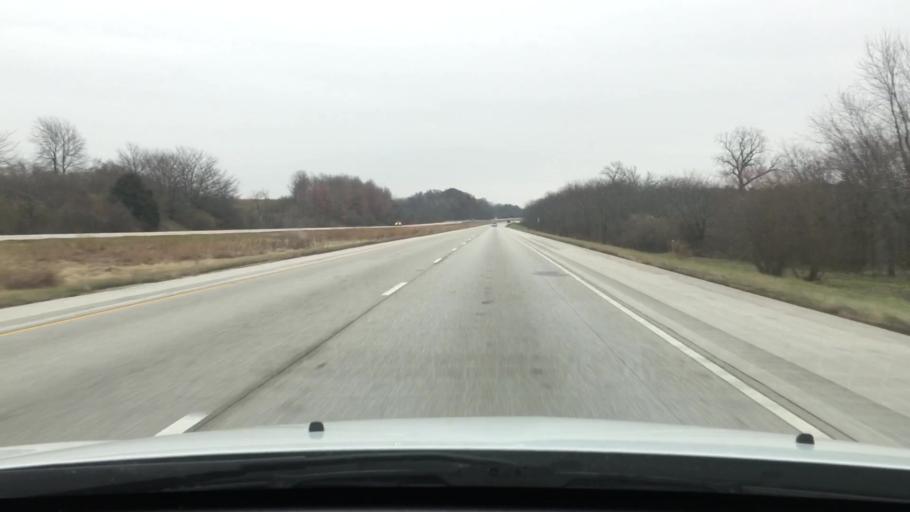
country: US
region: Illinois
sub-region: Scott County
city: Winchester
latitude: 39.6812
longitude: -90.4020
